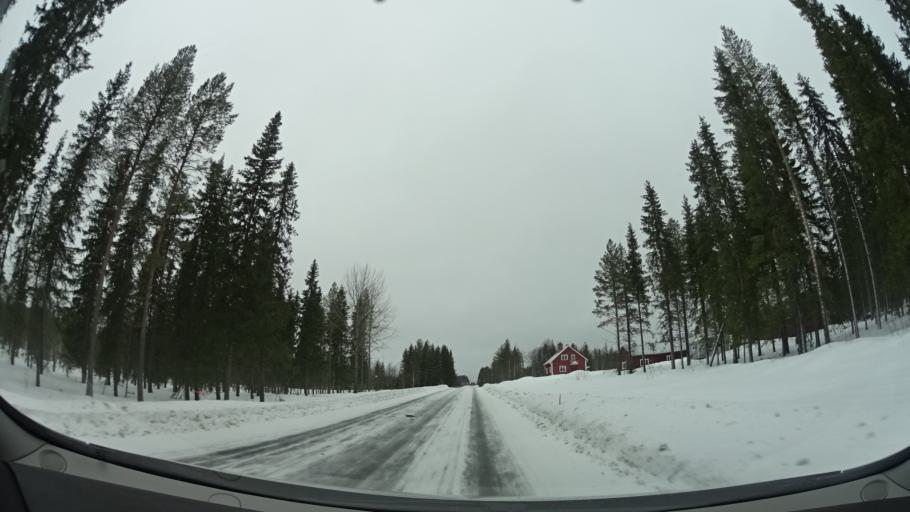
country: SE
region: Vaesterbotten
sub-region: Mala Kommun
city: Mala
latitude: 65.0928
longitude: 18.9409
